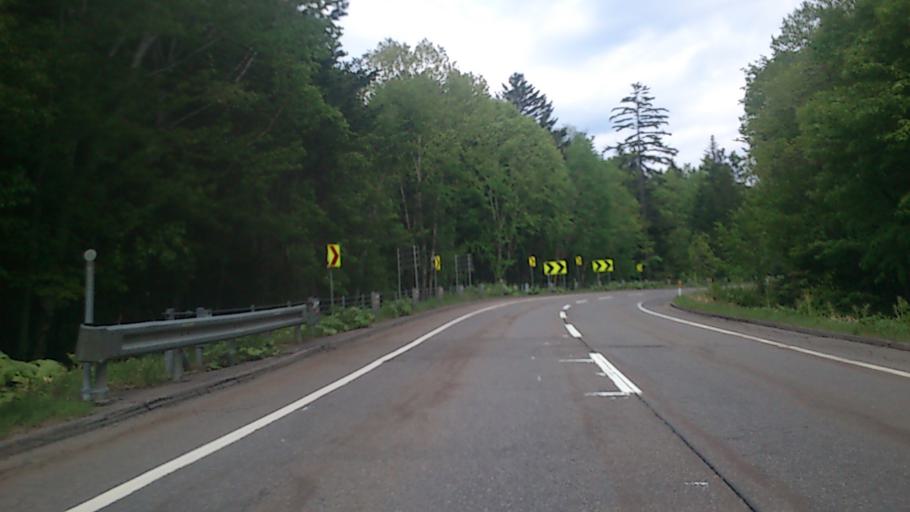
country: JP
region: Hokkaido
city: Kitami
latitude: 43.4072
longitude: 143.9470
